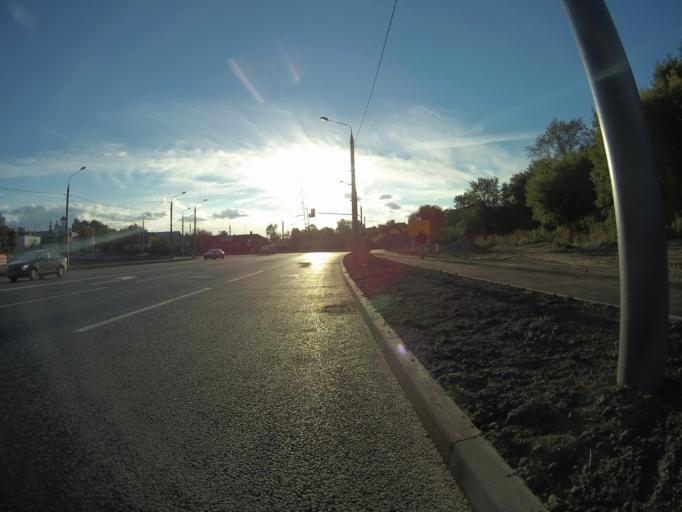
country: RU
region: Vladimir
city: Vladimir
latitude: 56.1339
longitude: 40.4037
